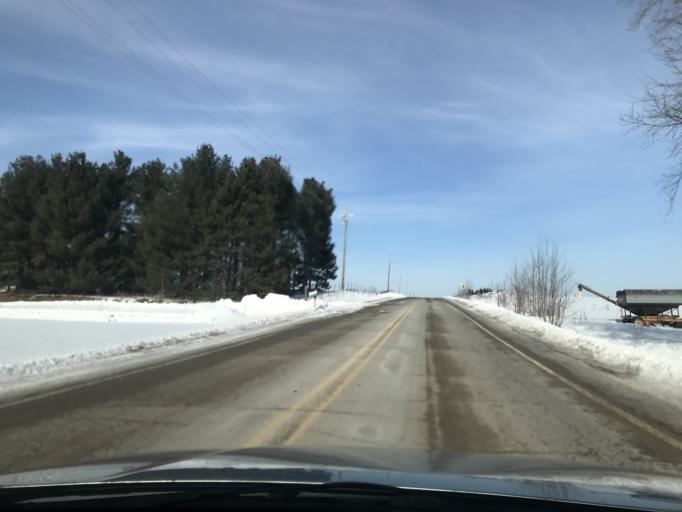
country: US
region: Wisconsin
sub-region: Oconto County
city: Oconto Falls
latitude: 45.1219
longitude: -88.1781
